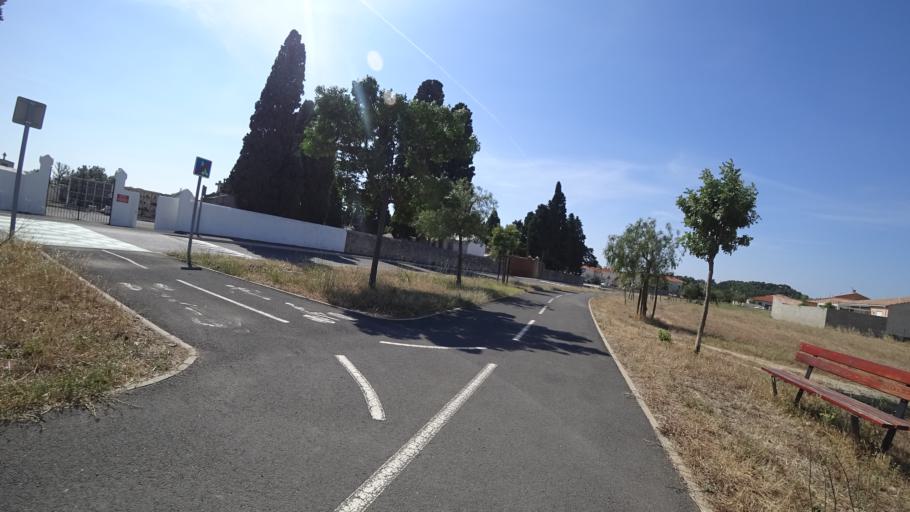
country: FR
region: Languedoc-Roussillon
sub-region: Departement des Pyrenees-Orientales
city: Peyrestortes
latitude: 42.7725
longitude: 2.8415
